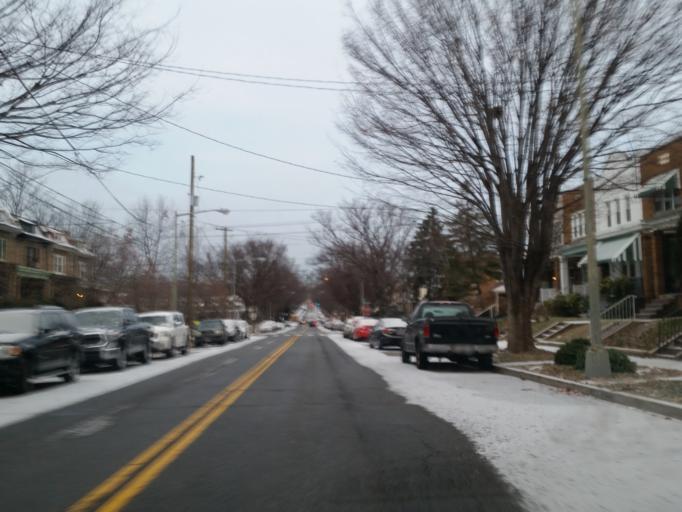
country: US
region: Maryland
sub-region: Montgomery County
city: Takoma Park
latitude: 38.9512
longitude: -77.0243
